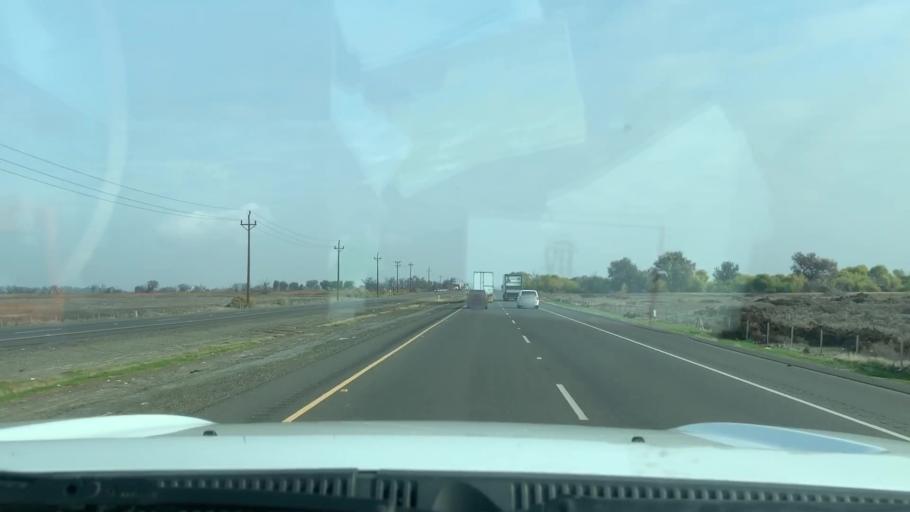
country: US
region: California
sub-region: Kings County
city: Lemoore Station
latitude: 36.2585
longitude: -119.8619
